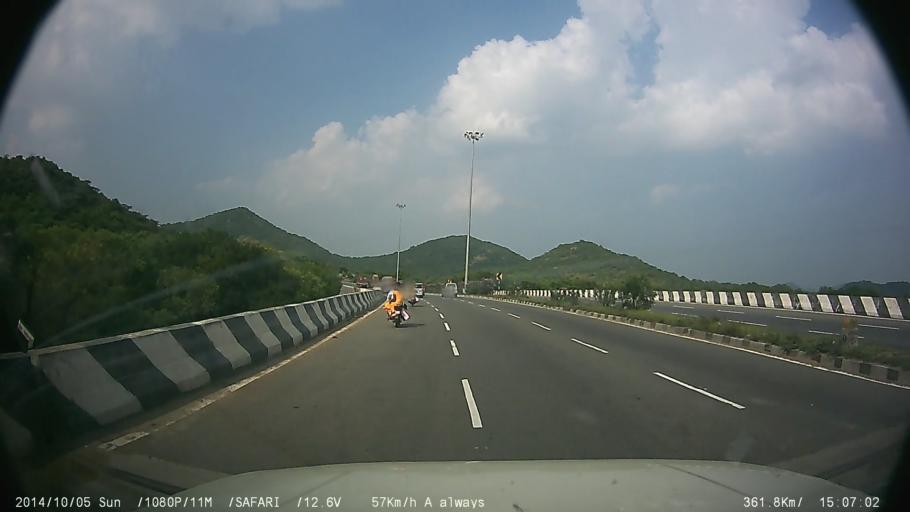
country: IN
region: Tamil Nadu
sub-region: Kancheepuram
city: Chengalpattu
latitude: 12.6586
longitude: 79.9596
